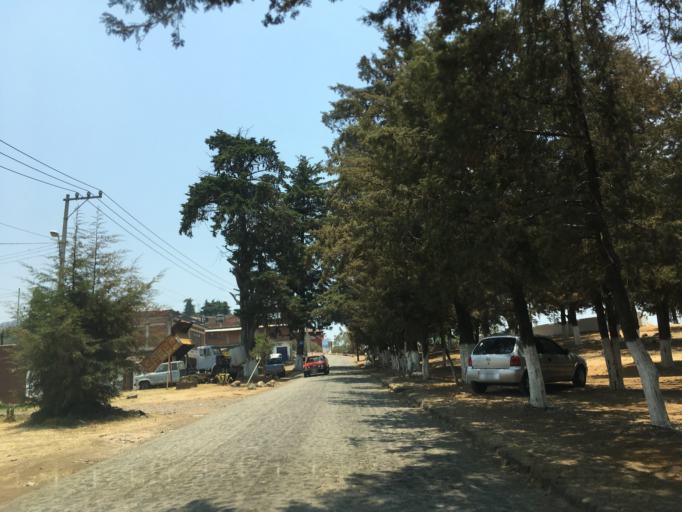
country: MX
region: Michoacan
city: Patzcuaro
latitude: 19.5153
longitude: -101.6214
